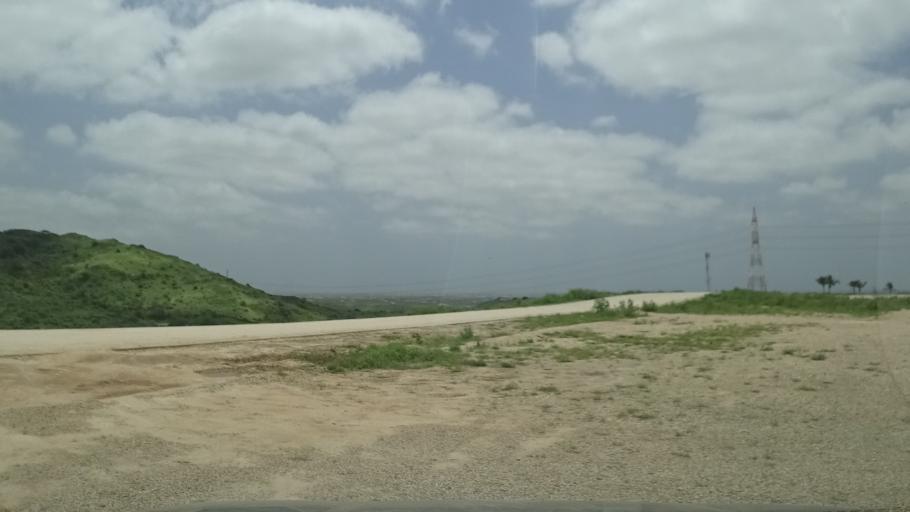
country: OM
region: Zufar
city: Salalah
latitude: 17.1477
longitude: 54.1777
